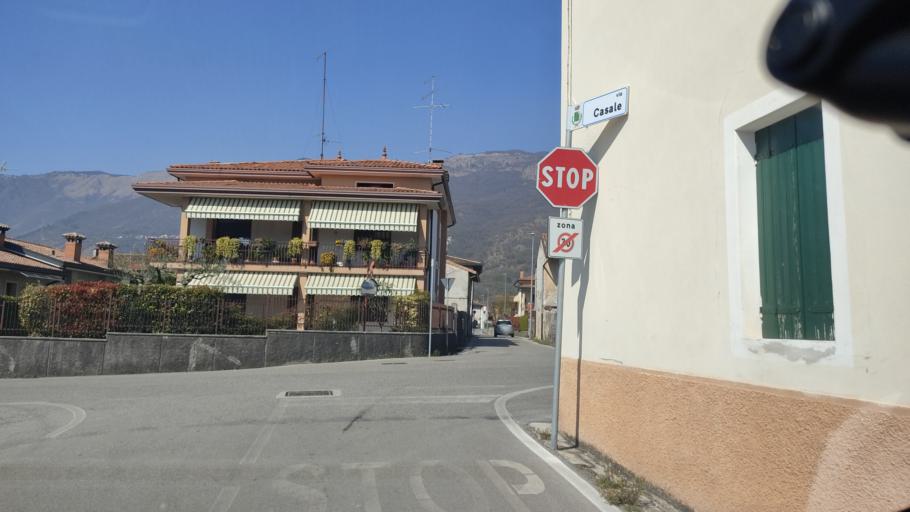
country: IT
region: Friuli Venezia Giulia
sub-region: Provincia di Pordenone
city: Budoia
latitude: 46.0447
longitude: 12.5322
